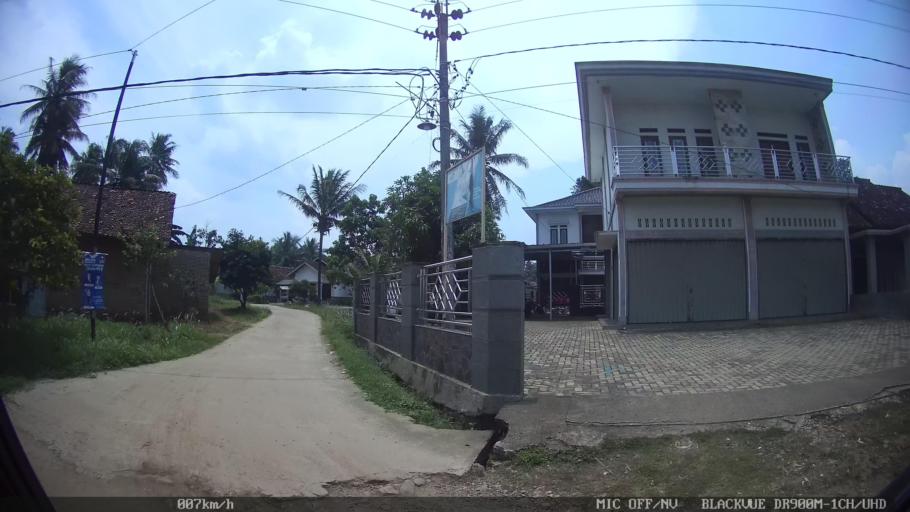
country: ID
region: Lampung
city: Natar
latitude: -5.3118
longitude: 105.2165
